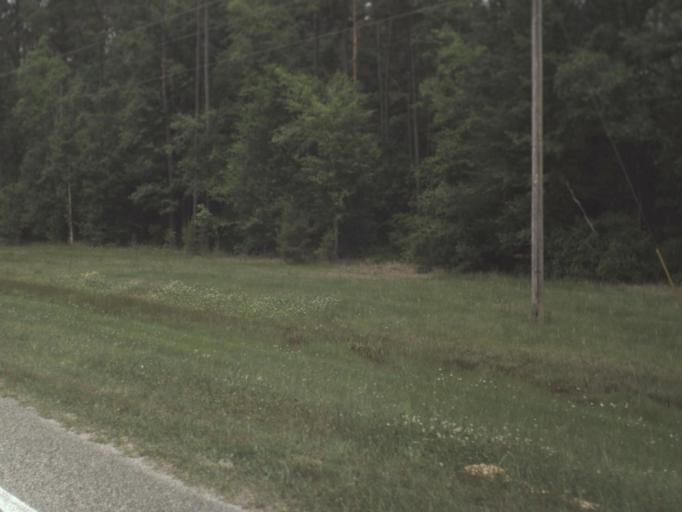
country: US
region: Florida
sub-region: Clay County
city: Middleburg
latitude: 30.0916
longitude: -81.8502
